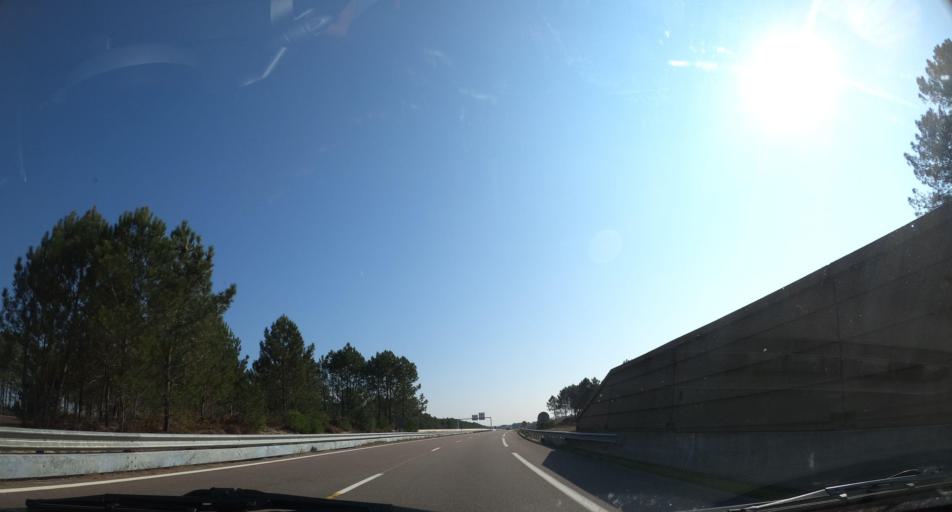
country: FR
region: Aquitaine
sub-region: Departement des Landes
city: Saint-Geours-de-Maremne
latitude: 43.6968
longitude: -1.2265
